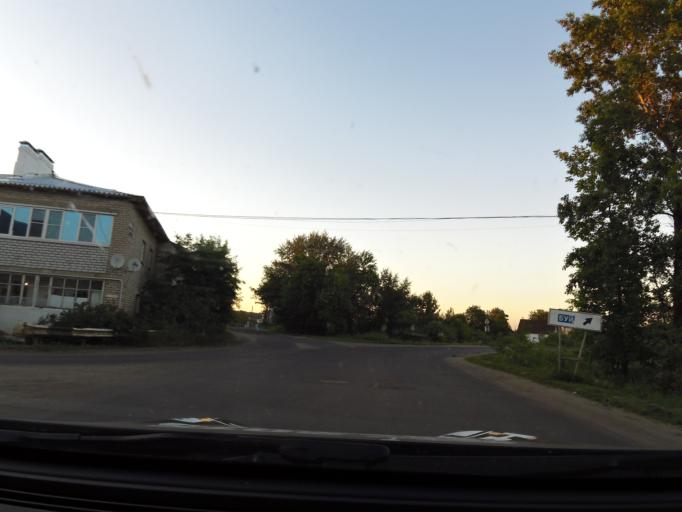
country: RU
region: Jaroslavl
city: Lyubim
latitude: 58.3600
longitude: 40.7004
